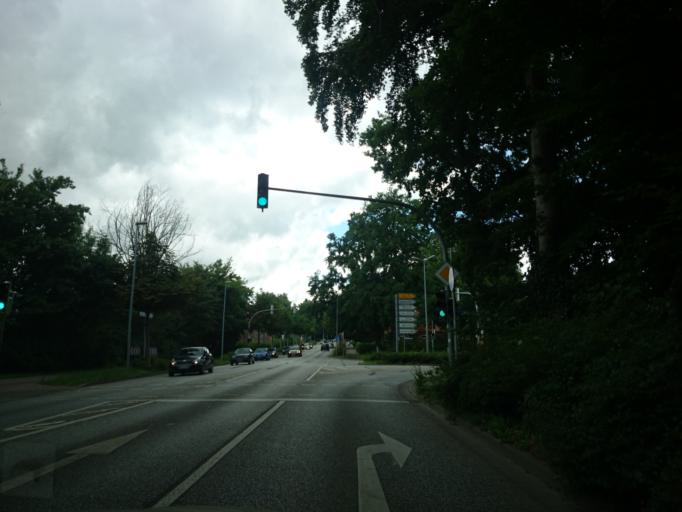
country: DE
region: Mecklenburg-Vorpommern
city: Wismar
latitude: 53.8824
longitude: 11.4613
